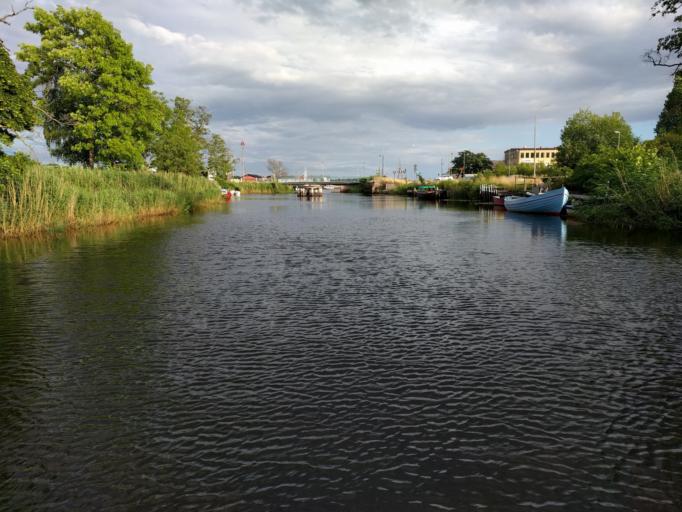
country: SE
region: Blekinge
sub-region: Ronneby Kommun
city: Ronneby
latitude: 56.1779
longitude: 15.2993
